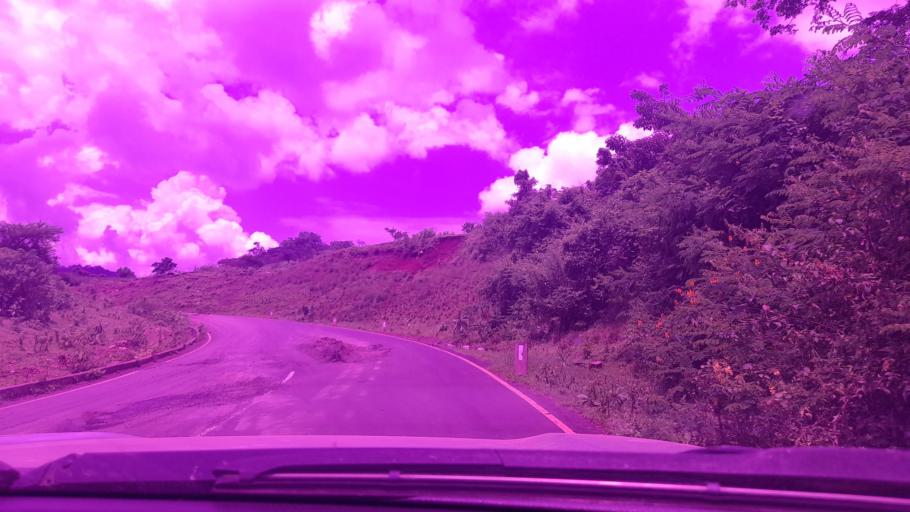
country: ET
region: Oromiya
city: Metu
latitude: 8.3293
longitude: 35.7600
